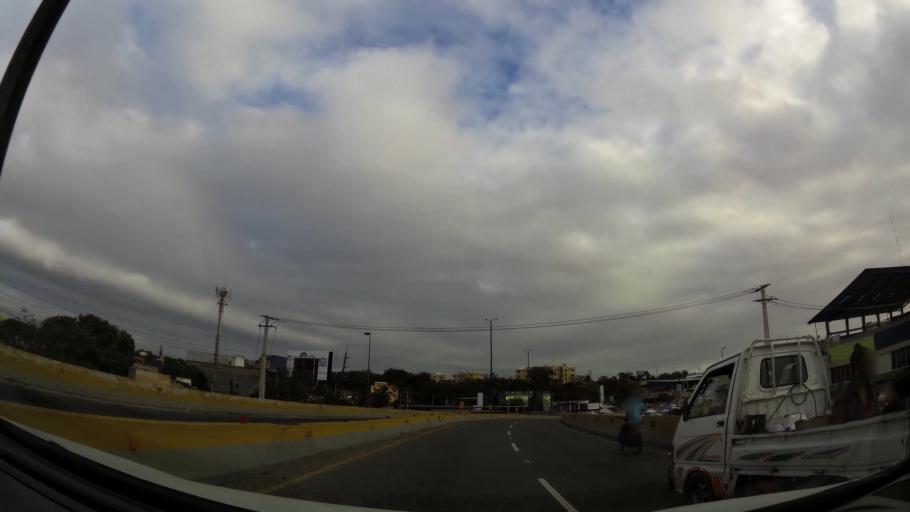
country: DO
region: San Cristobal
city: El Carril
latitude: 18.4280
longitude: -69.9903
